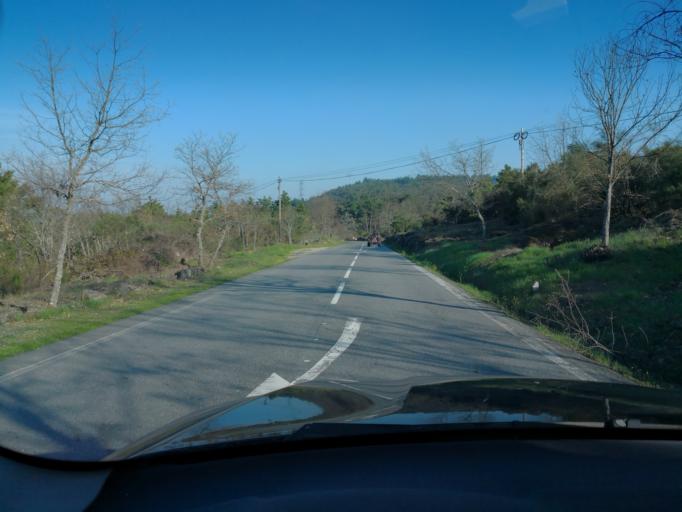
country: PT
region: Vila Real
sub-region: Sabrosa
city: Sabrosa
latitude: 41.3594
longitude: -7.6339
